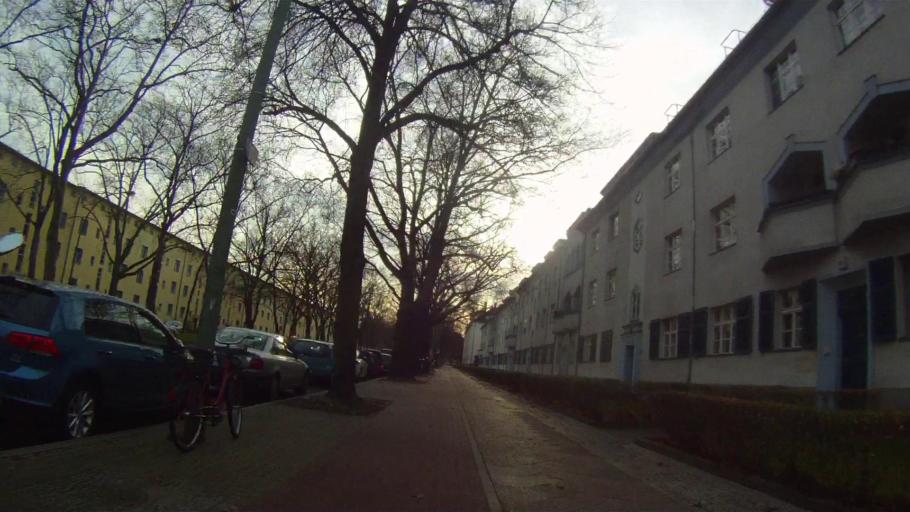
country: DE
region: Berlin
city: Buckow
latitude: 52.4477
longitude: 13.4540
